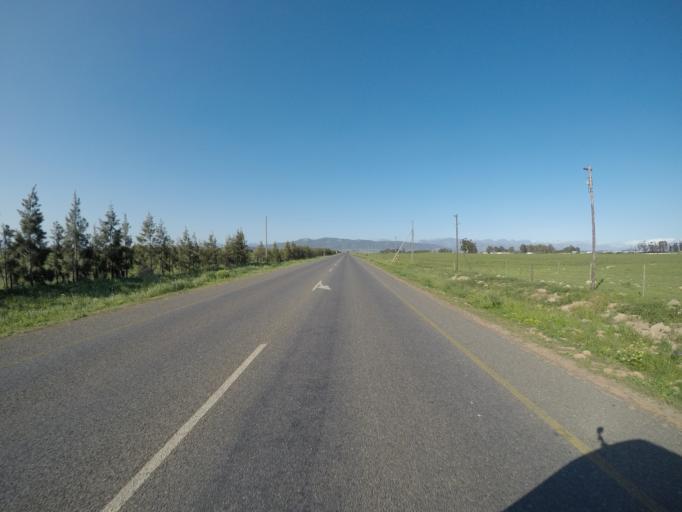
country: ZA
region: Western Cape
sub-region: City of Cape Town
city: Kraaifontein
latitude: -33.7644
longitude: 18.7954
